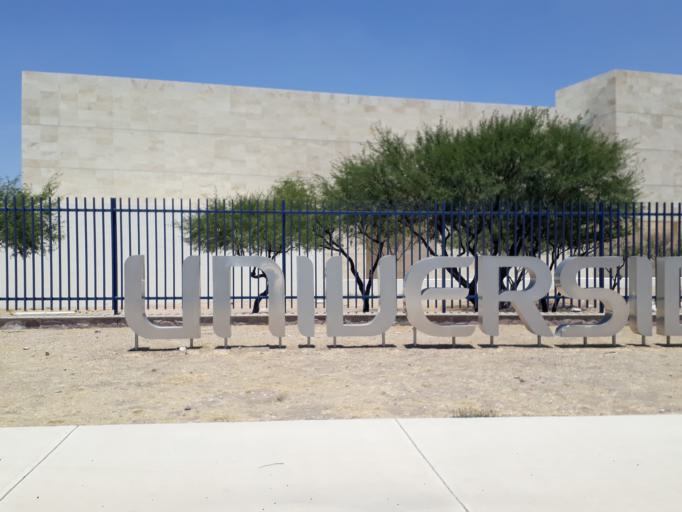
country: MX
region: Aguascalientes
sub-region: Aguascalientes
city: San Sebastian [Fraccionamiento]
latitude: 21.7933
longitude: -102.2873
